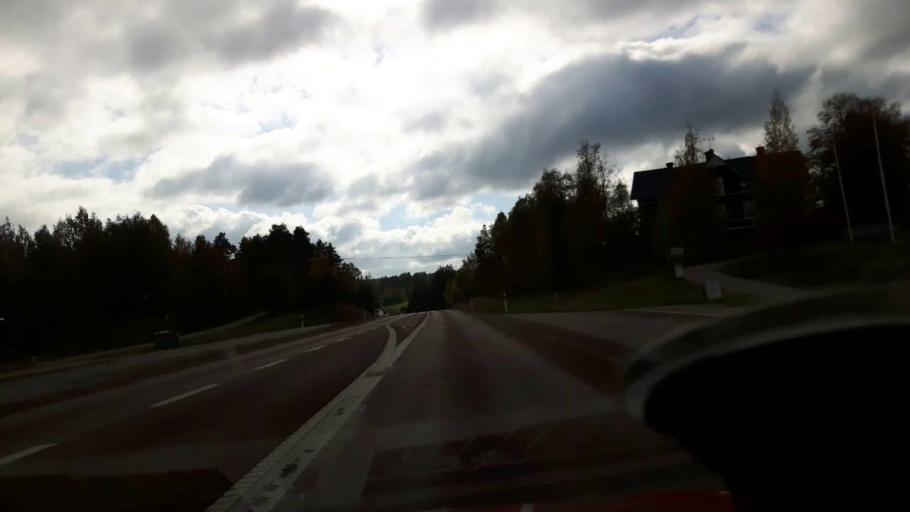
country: SE
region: Gaevleborg
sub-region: Ljusdals Kommun
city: Jaervsoe
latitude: 61.6717
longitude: 16.1456
